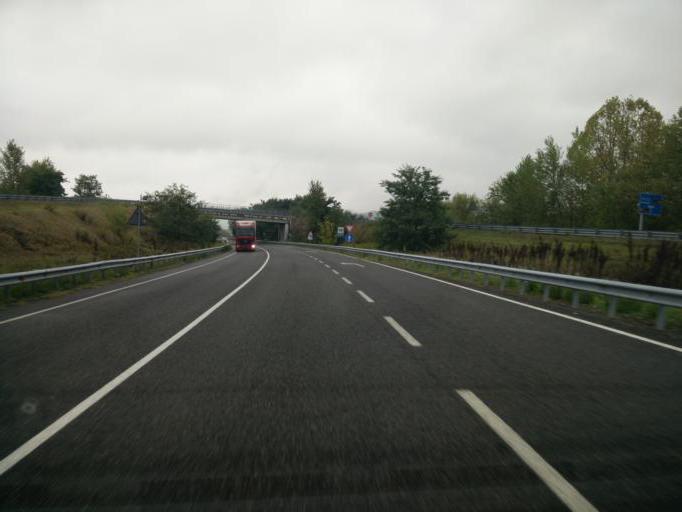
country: IT
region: Emilia-Romagna
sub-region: Provincia di Bologna
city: Borgonuovo
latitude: 44.4297
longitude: 11.2766
